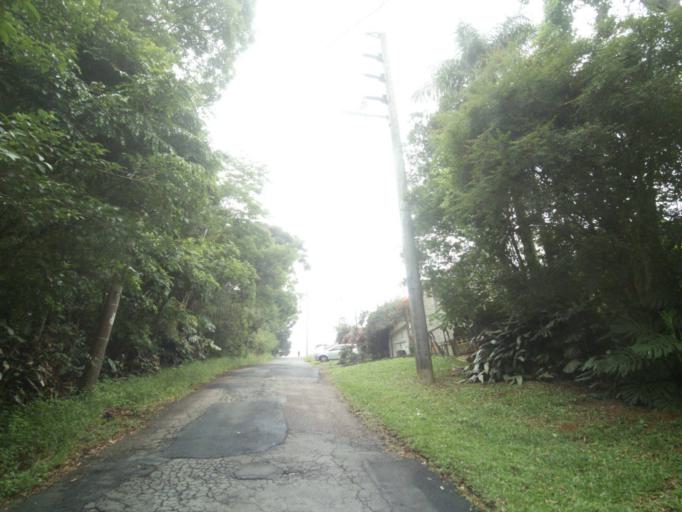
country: BR
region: Parana
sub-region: Curitiba
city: Curitiba
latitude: -25.4074
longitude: -49.3003
